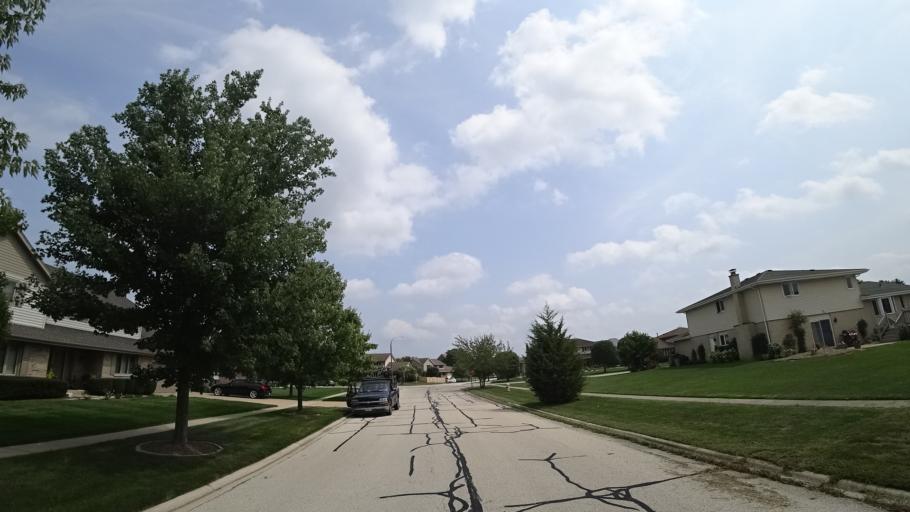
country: US
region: Illinois
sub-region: Will County
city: Goodings Grove
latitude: 41.6209
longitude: -87.9089
